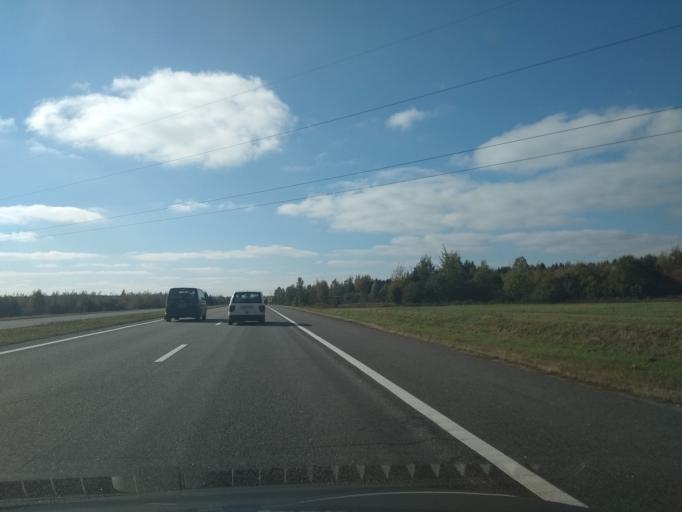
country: BY
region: Minsk
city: Haradzyeya
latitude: 53.3900
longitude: 26.5249
